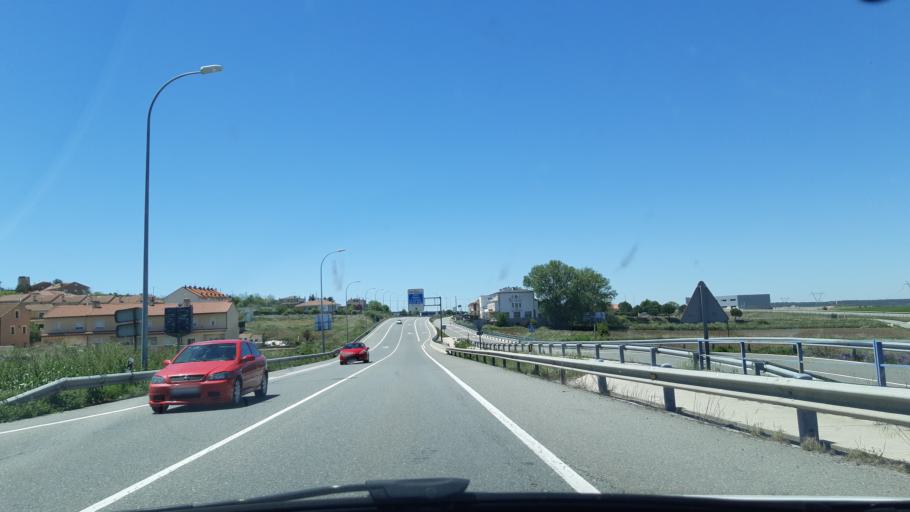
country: ES
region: Castille and Leon
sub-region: Provincia de Segovia
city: Villacastin
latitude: 40.7825
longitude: -4.4135
